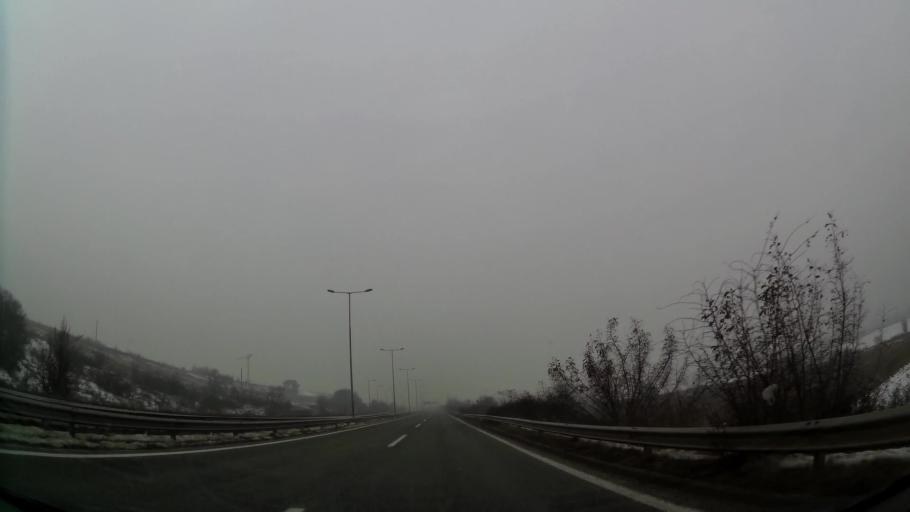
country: MK
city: Miladinovci
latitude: 41.9641
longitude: 21.6376
